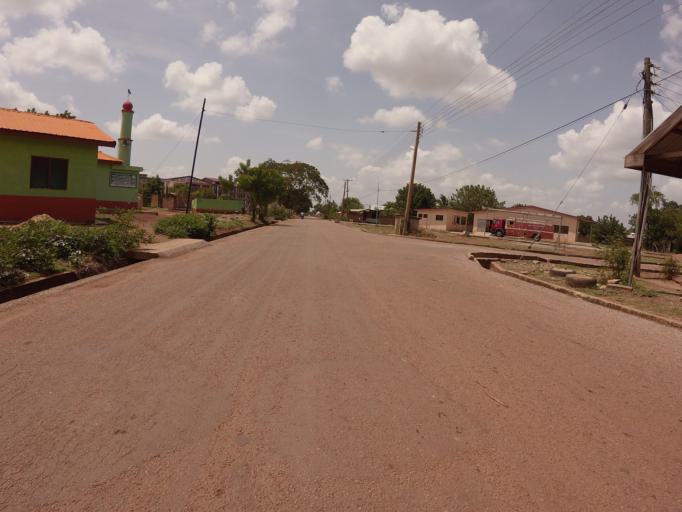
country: GH
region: Northern
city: Tamale
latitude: 9.3906
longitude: -0.8240
